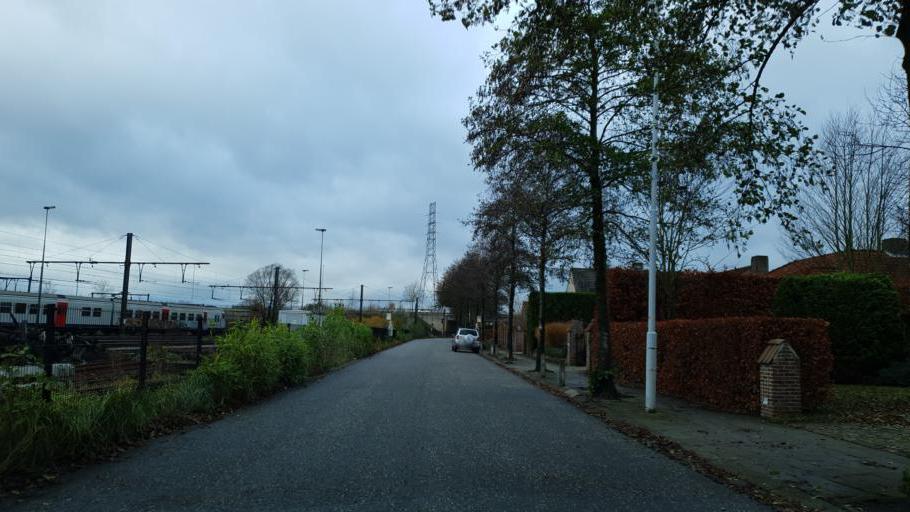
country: BE
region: Flanders
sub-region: Provincie Antwerpen
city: Lier
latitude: 51.1358
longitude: 4.5532
